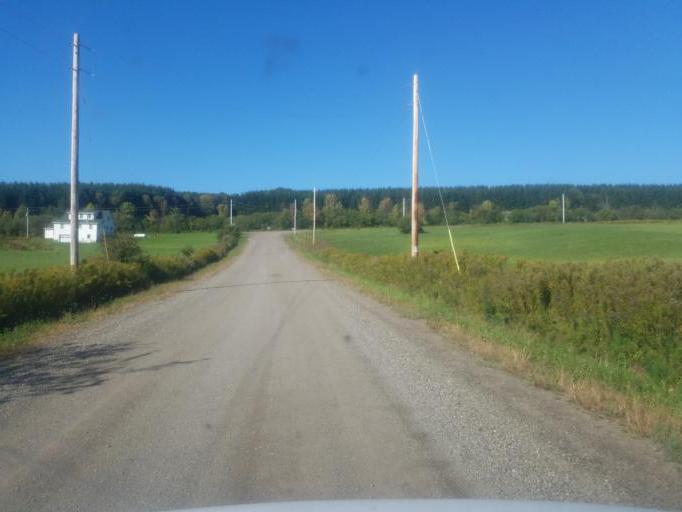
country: US
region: New York
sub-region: Allegany County
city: Cuba
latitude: 42.2374
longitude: -78.2297
